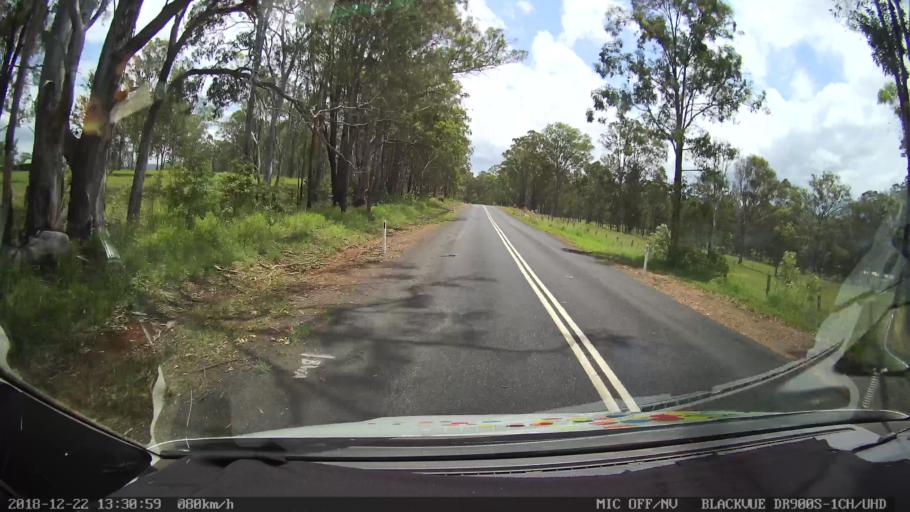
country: AU
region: New South Wales
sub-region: Clarence Valley
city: Coutts Crossing
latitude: -29.8529
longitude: 152.8584
